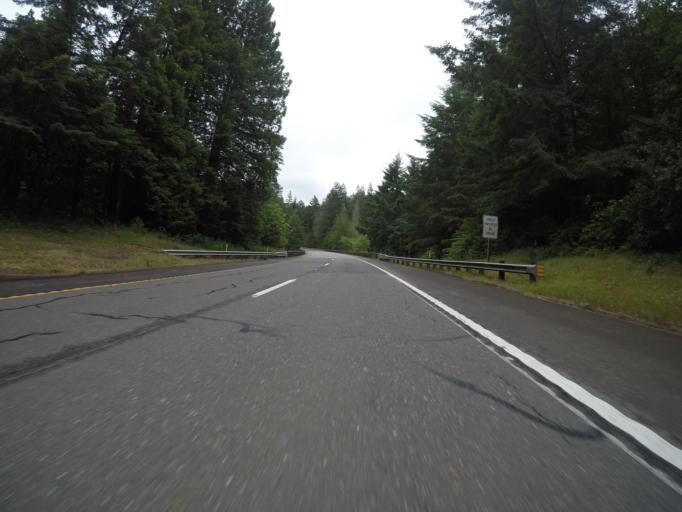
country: US
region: California
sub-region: Humboldt County
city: Rio Dell
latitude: 40.4410
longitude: -124.0383
